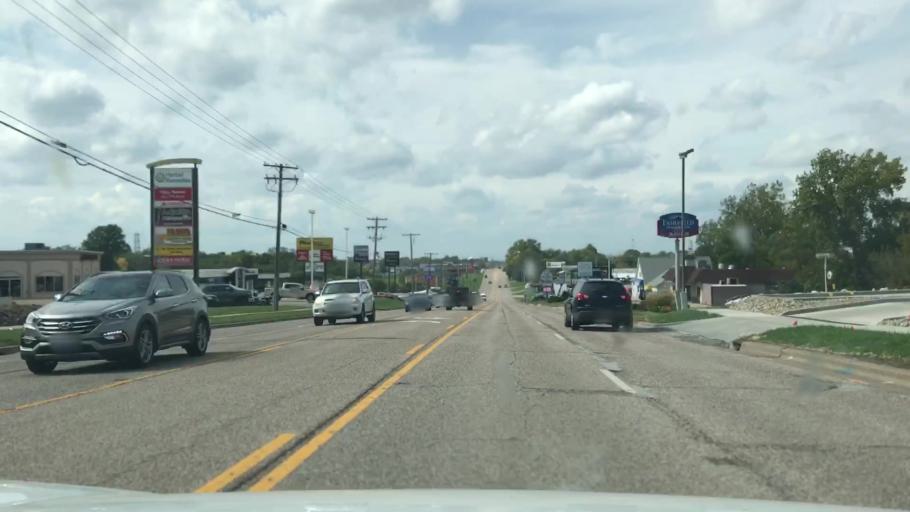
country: US
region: Illinois
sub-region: Adams County
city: Quincy
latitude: 39.9351
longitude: -91.3442
